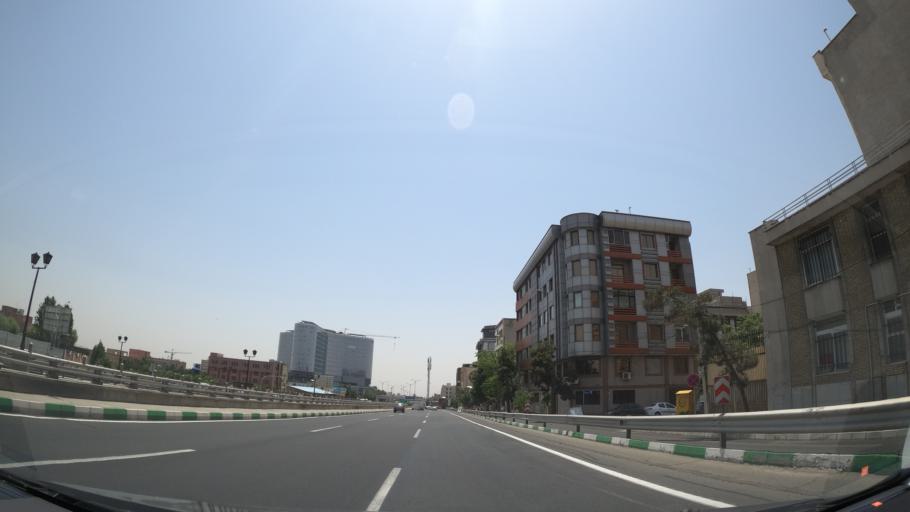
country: IR
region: Tehran
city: Tehran
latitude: 35.7129
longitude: 51.3776
